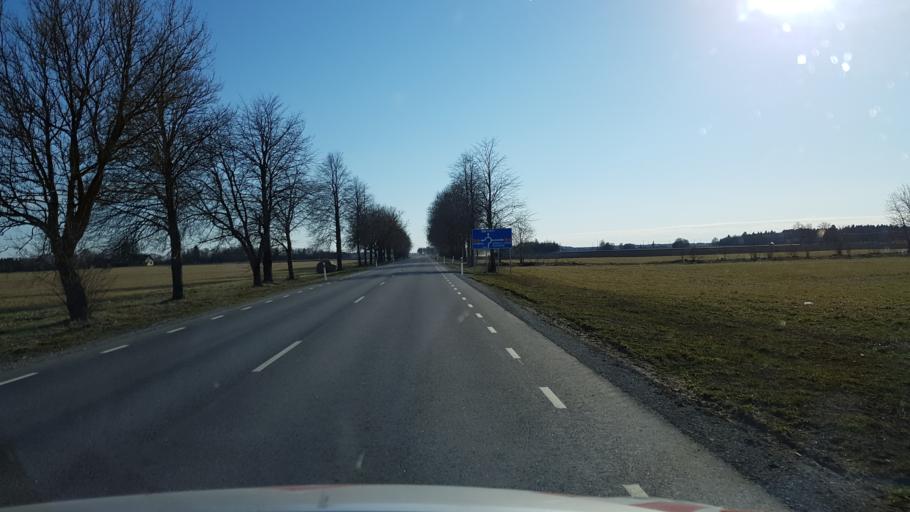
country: EE
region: Ida-Virumaa
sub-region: Johvi vald
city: Johvi
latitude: 59.3468
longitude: 27.3683
